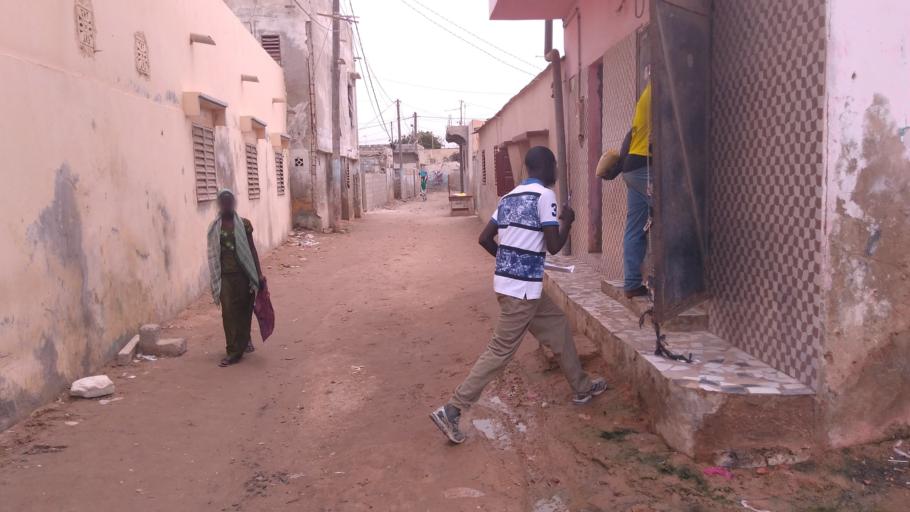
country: SN
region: Dakar
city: Pikine
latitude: 14.6883
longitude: -17.2273
